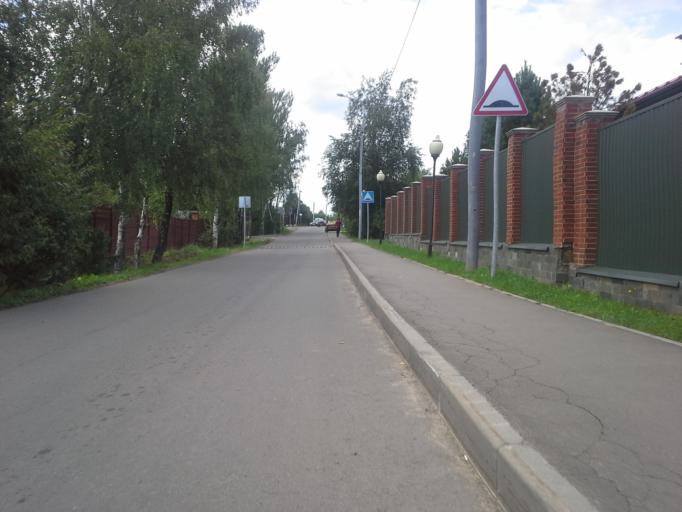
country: RU
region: Moskovskaya
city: Odintsovo
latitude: 55.6433
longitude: 37.2690
